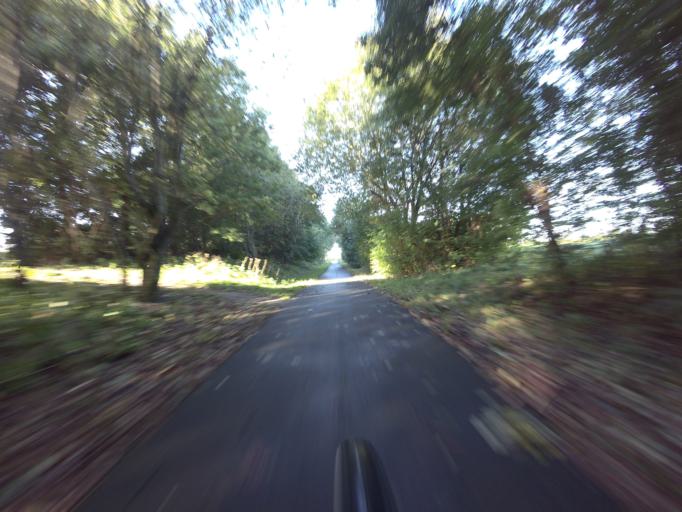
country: DK
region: Central Jutland
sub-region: Viborg Kommune
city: Bjerringbro
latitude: 56.4885
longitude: 9.6322
